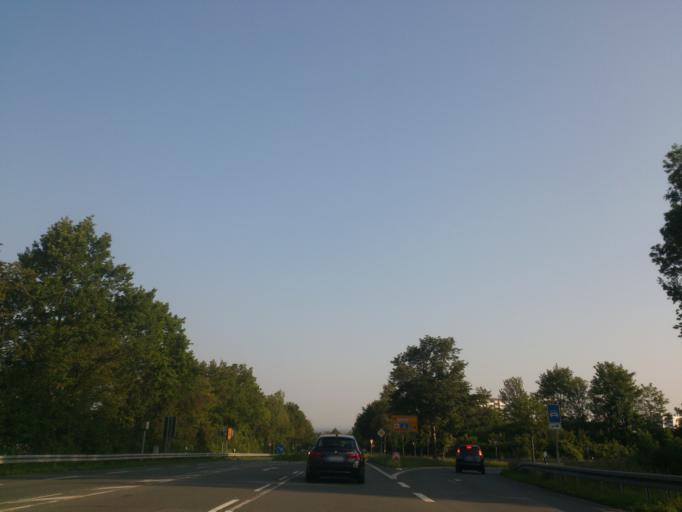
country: DE
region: North Rhine-Westphalia
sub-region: Regierungsbezirk Detmold
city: Paderborn
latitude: 51.7027
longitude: 8.7806
